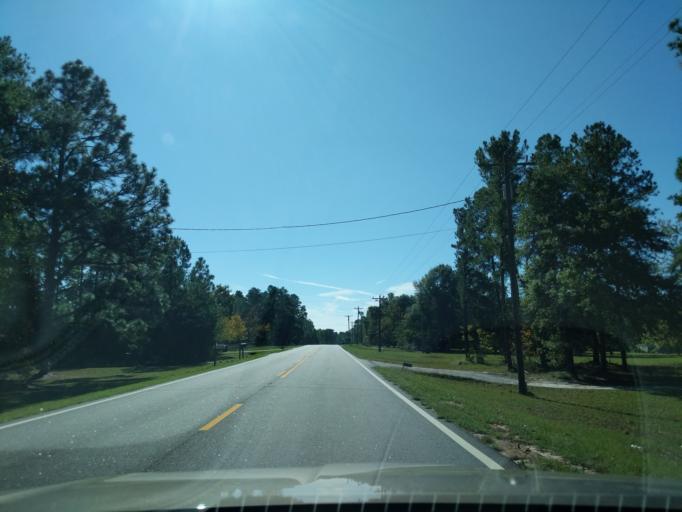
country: US
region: Georgia
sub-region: Richmond County
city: Hephzibah
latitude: 33.2640
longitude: -82.0089
